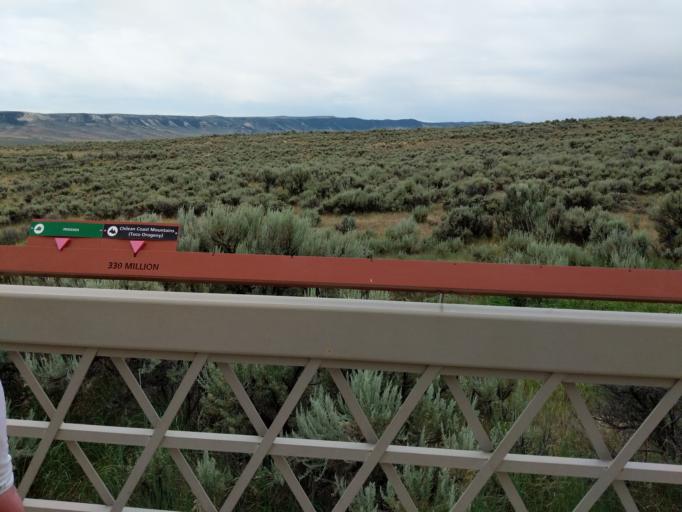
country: US
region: Wyoming
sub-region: Lincoln County
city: Kemmerer
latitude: 41.8364
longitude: -110.7706
